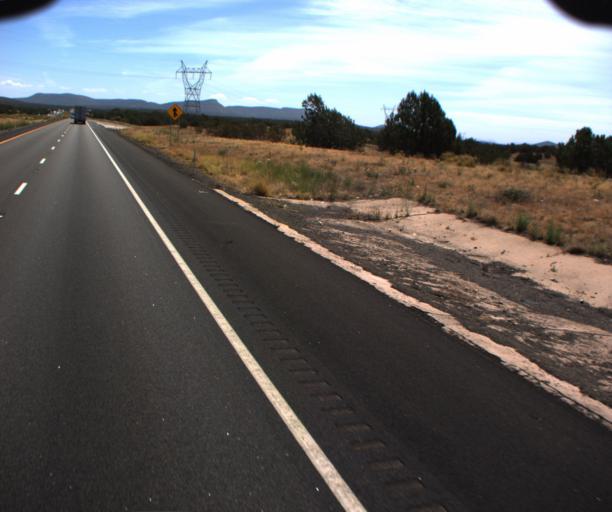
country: US
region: Arizona
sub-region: Mohave County
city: Peach Springs
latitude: 35.1907
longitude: -113.3638
